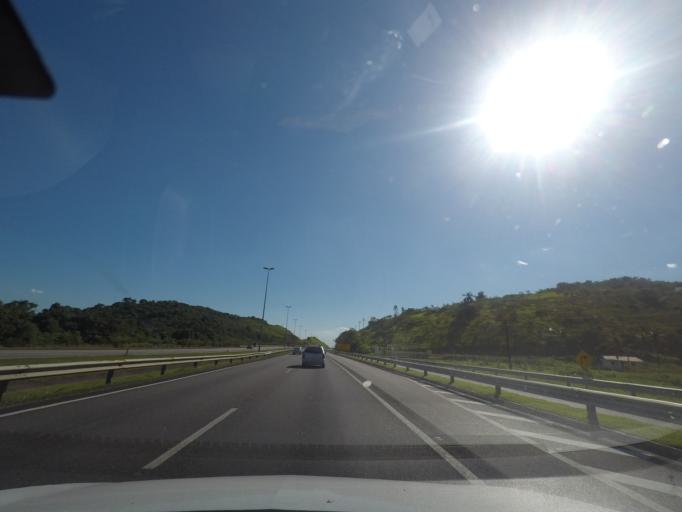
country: BR
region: Rio de Janeiro
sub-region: Guapimirim
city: Guapimirim
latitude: -22.6395
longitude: -43.0618
